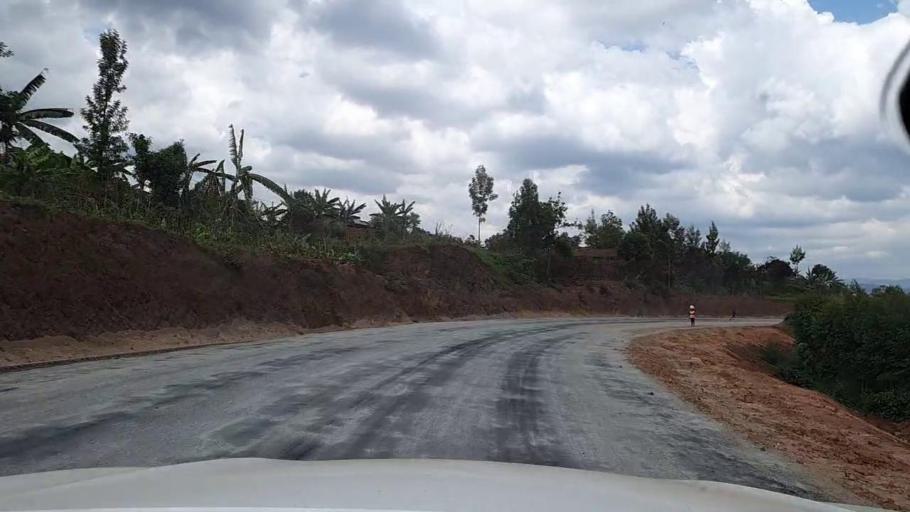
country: RW
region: Southern Province
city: Butare
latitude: -2.6984
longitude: 29.5658
